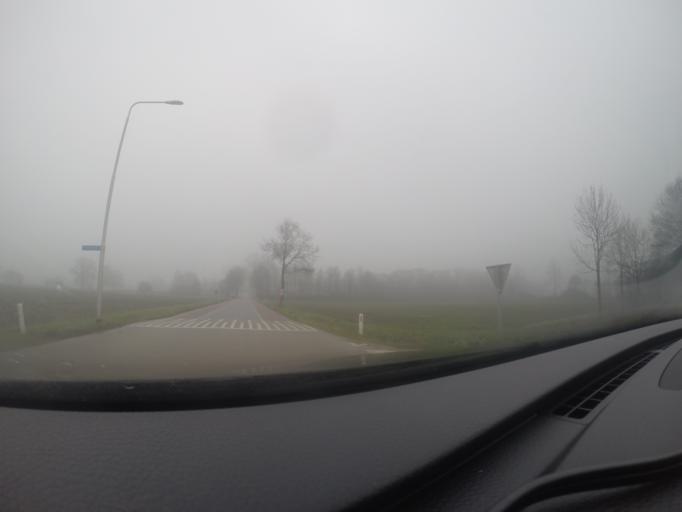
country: NL
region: Gelderland
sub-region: Gemeente Lochem
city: Barchem
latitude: 52.0588
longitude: 6.4681
